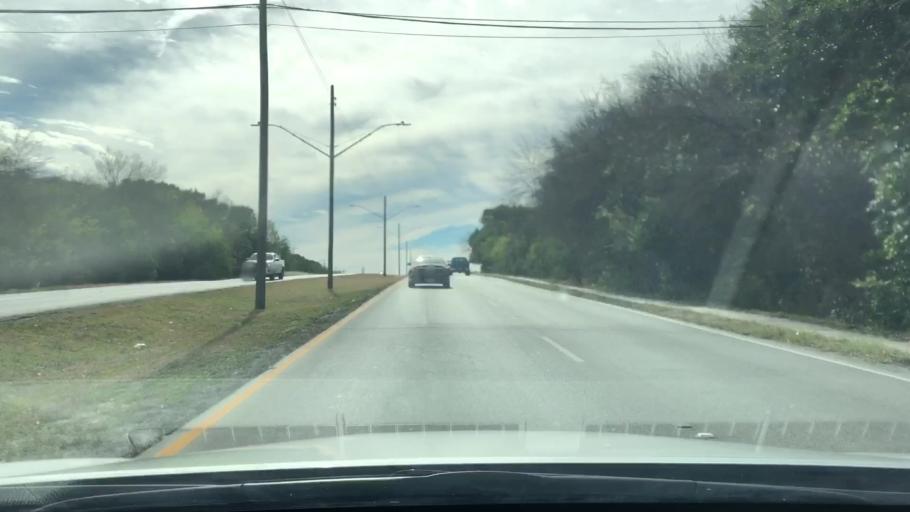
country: US
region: Texas
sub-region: Bexar County
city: Terrell Hills
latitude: 29.5002
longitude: -98.4347
